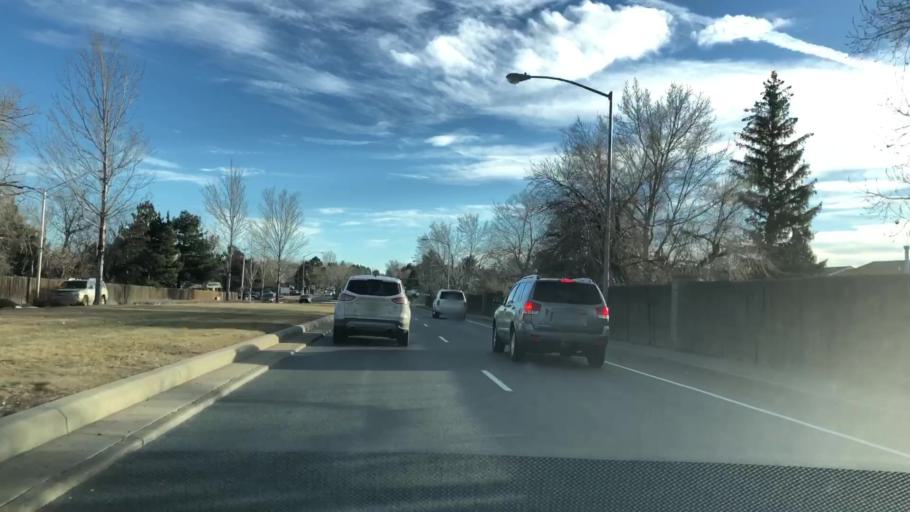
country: US
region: Colorado
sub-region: Arapahoe County
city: Dove Valley
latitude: 39.6421
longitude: -104.7918
